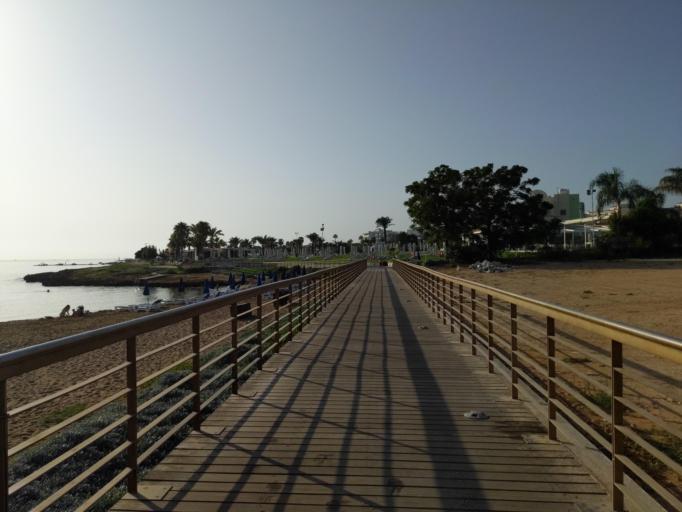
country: CY
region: Ammochostos
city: Protaras
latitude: 35.0309
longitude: 34.0437
